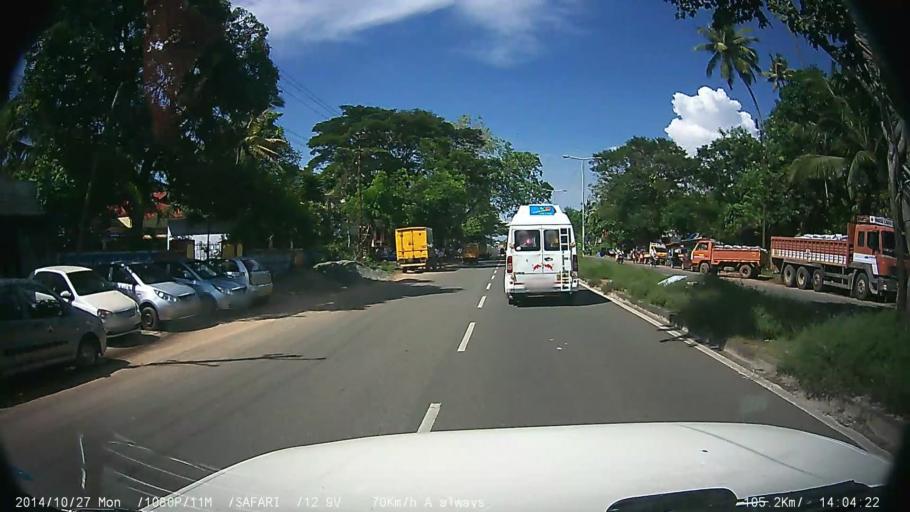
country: IN
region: Kerala
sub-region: Alappuzha
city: Vayalar
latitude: 9.7316
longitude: 76.3188
